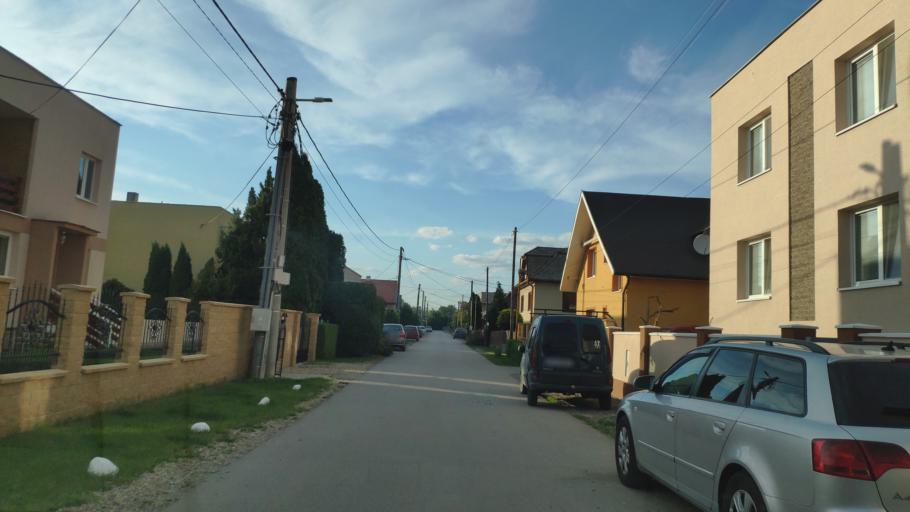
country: SK
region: Kosicky
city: Kosice
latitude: 48.6177
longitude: 21.3230
